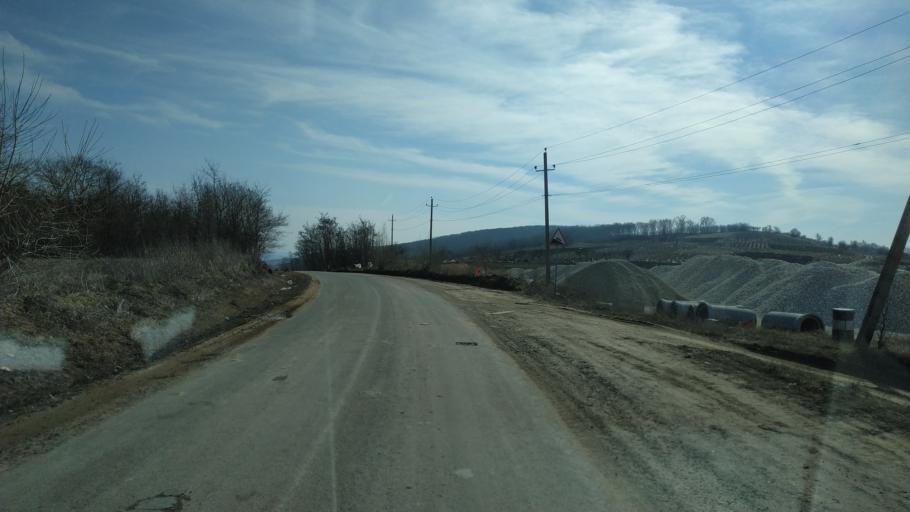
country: MD
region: Nisporeni
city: Nisporeni
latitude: 47.1921
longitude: 28.0667
